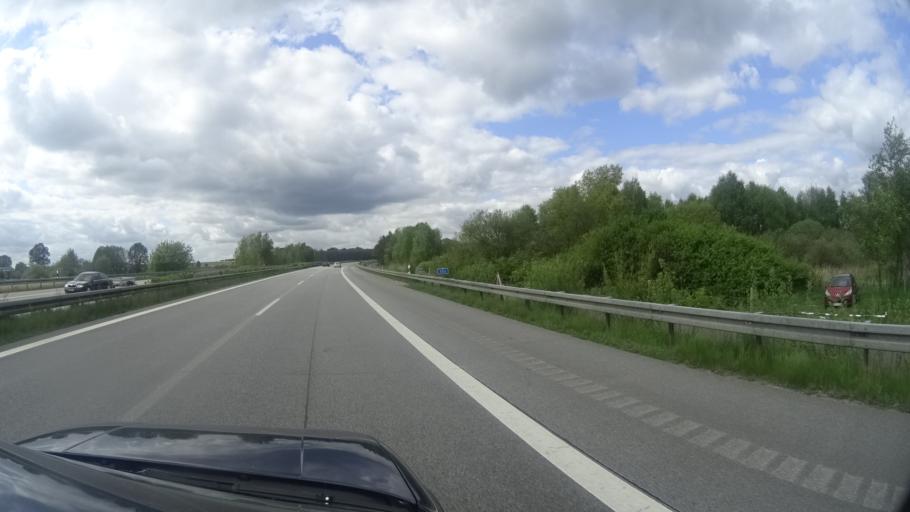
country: DE
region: Mecklenburg-Vorpommern
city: Malchow
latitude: 53.5140
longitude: 12.3609
